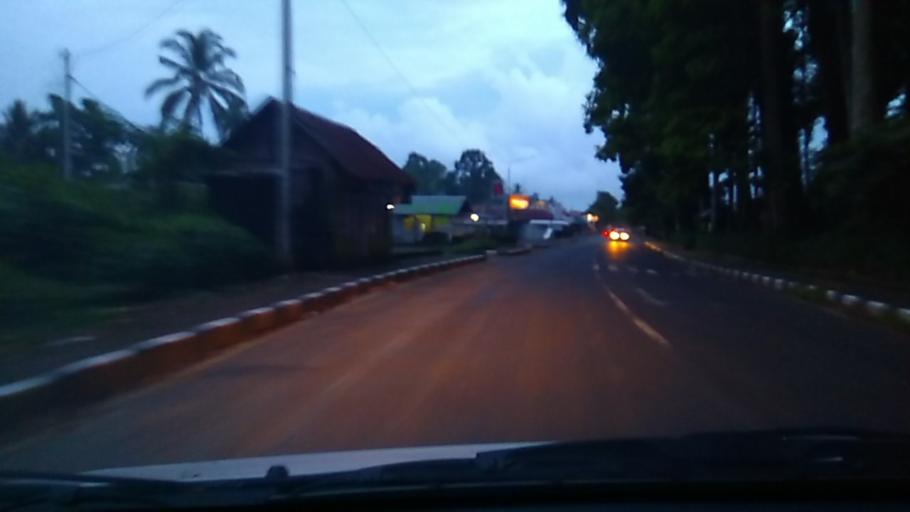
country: ID
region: Bali
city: Brahmana
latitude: -8.4801
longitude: 115.2088
